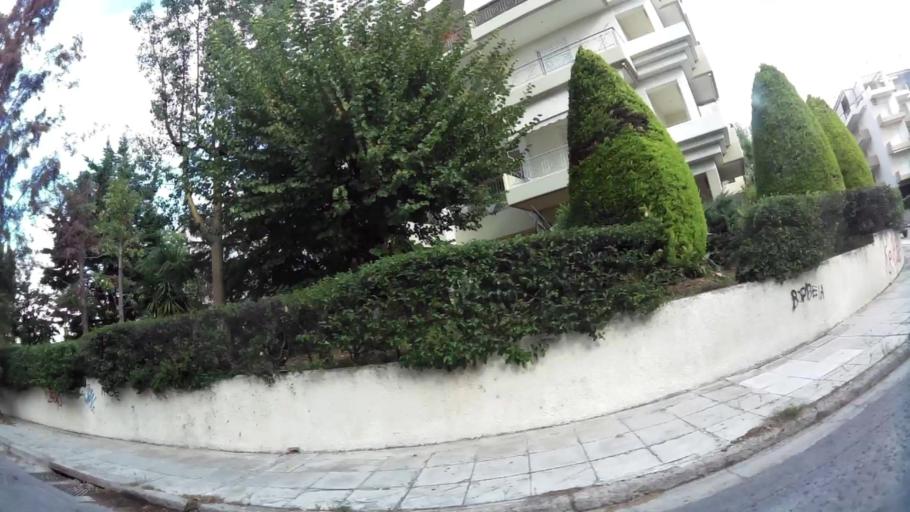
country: GR
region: Attica
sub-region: Nomarchia Athinas
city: Melissia
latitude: 38.0581
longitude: 23.8334
